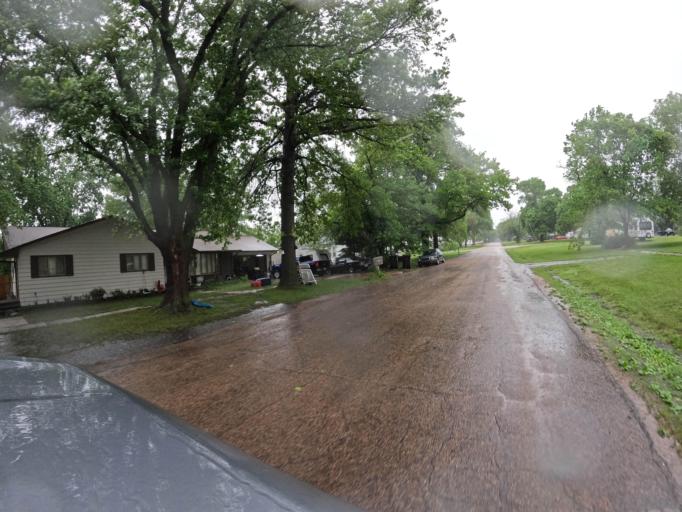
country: US
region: Nebraska
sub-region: Gage County
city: Wymore
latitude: 40.1176
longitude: -96.6688
